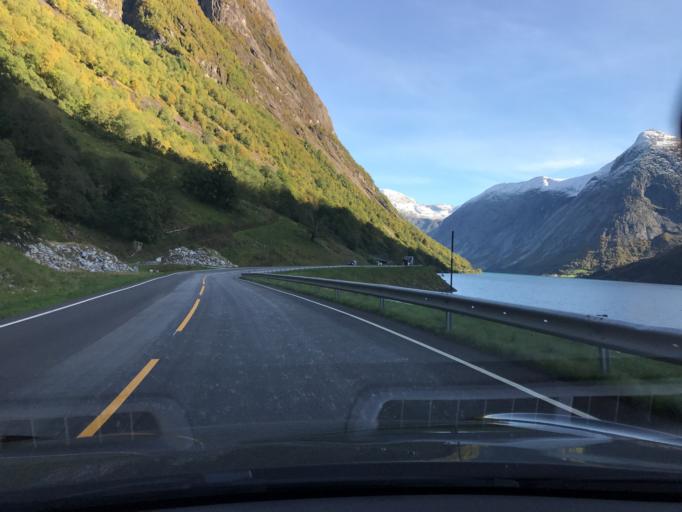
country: NO
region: Sogn og Fjordane
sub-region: Jolster
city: Skei
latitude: 61.5428
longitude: 6.5288
